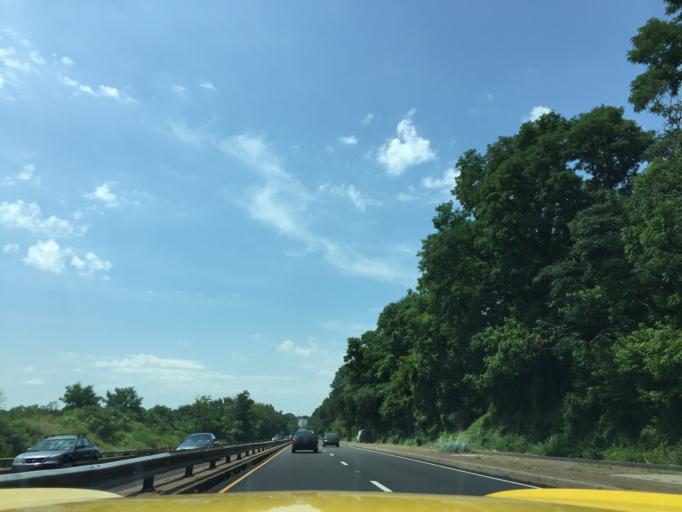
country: US
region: Pennsylvania
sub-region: Bucks County
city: Penndel
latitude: 40.1537
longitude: -74.9462
